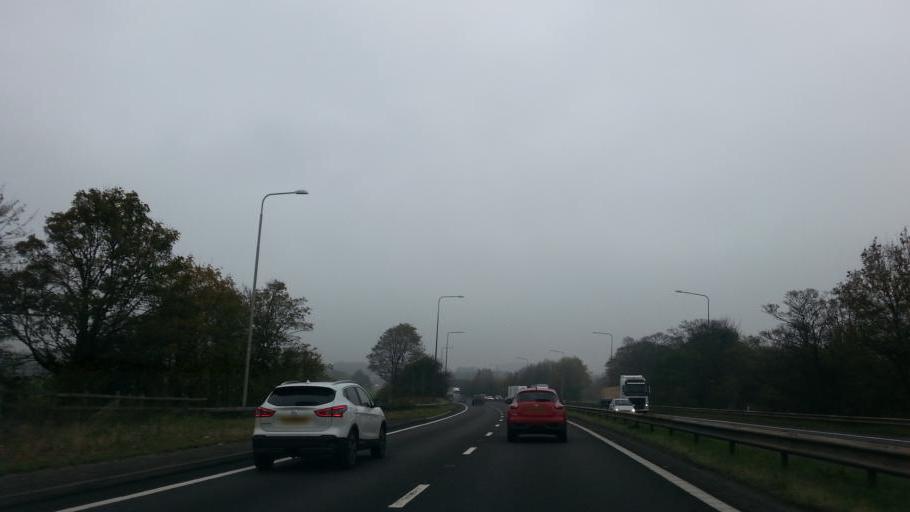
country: GB
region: England
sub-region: Doncaster
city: Campsall
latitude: 53.5977
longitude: -1.2171
